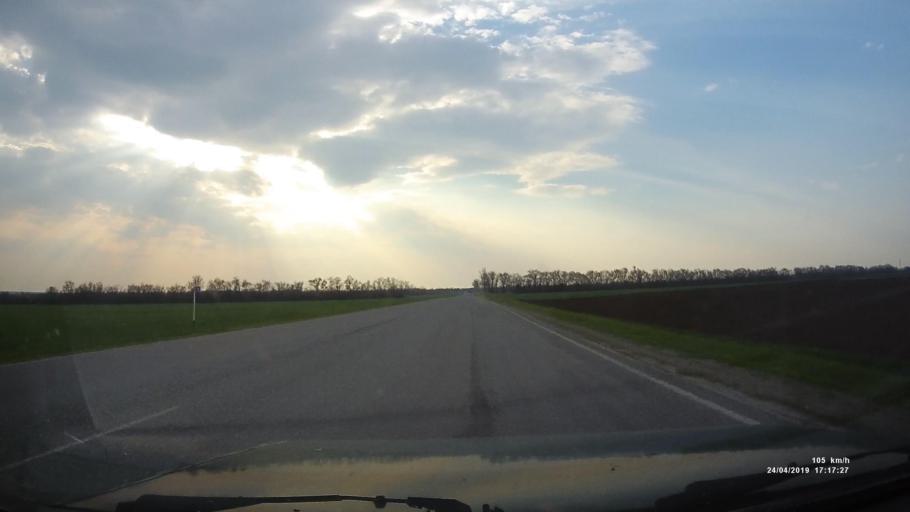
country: RU
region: Rostov
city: Gigant
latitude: 46.5066
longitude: 41.4060
